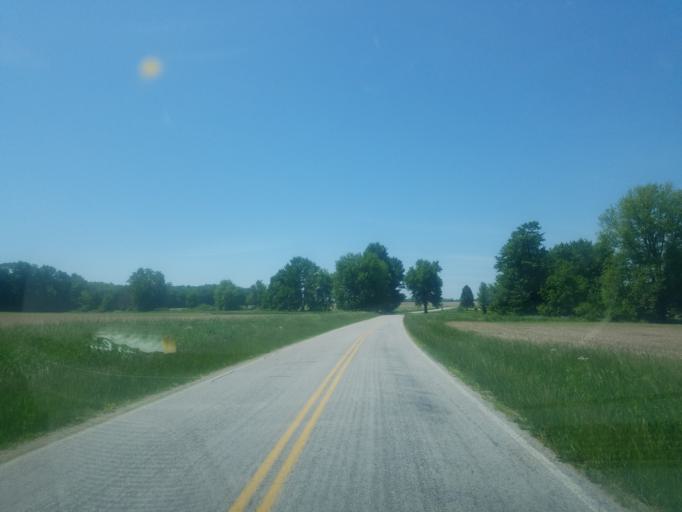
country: US
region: Ohio
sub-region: Huron County
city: New London
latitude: 41.1126
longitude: -82.4470
